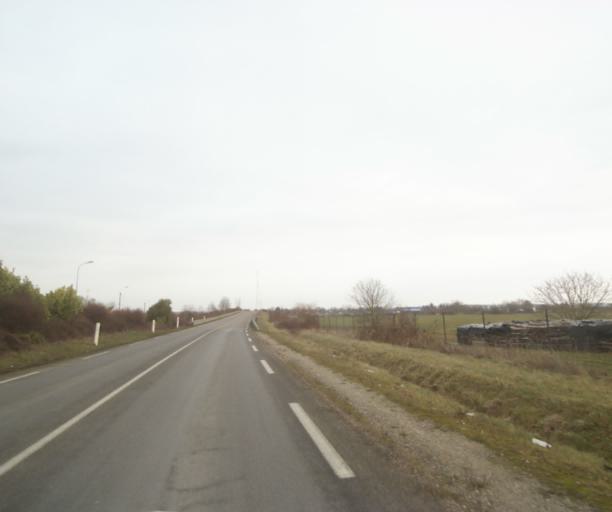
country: FR
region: Champagne-Ardenne
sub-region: Departement de la Haute-Marne
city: Saint-Dizier
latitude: 48.6251
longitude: 4.9308
